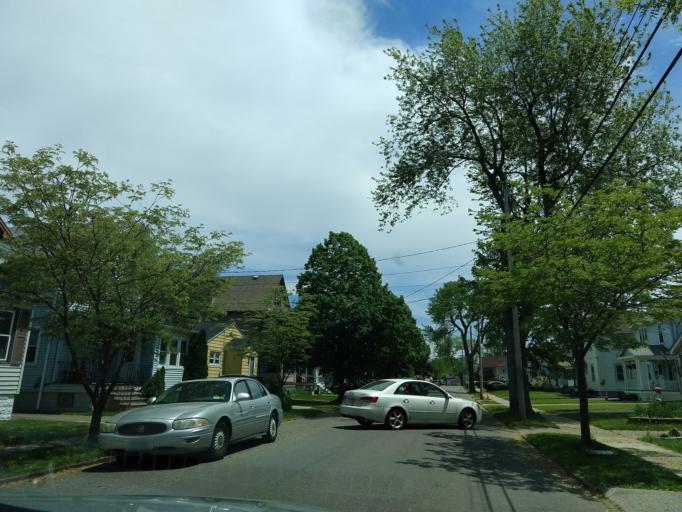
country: US
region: New York
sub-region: Erie County
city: Lackawanna
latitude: 42.8425
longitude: -78.8268
